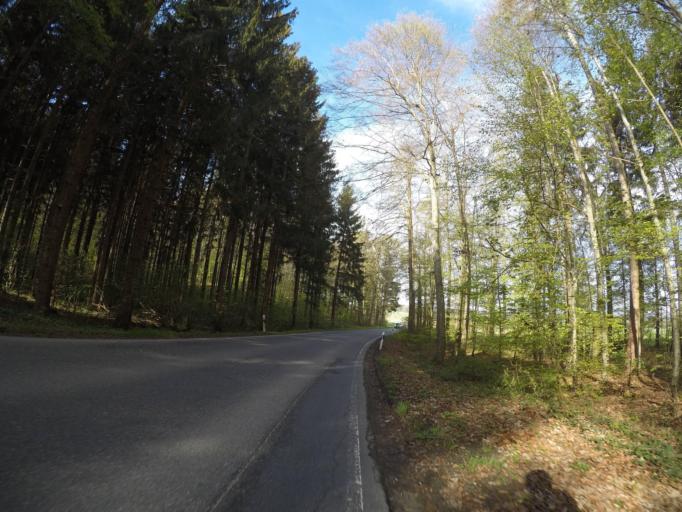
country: DE
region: Baden-Wuerttemberg
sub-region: Tuebingen Region
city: Bad Schussenried
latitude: 48.0068
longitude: 9.6337
